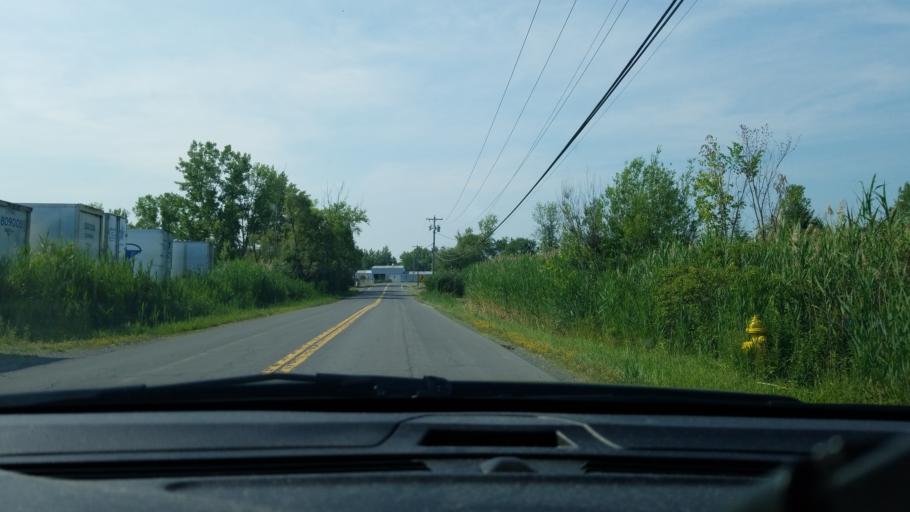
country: US
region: New York
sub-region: Onondaga County
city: North Syracuse
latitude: 43.1235
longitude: -76.0733
